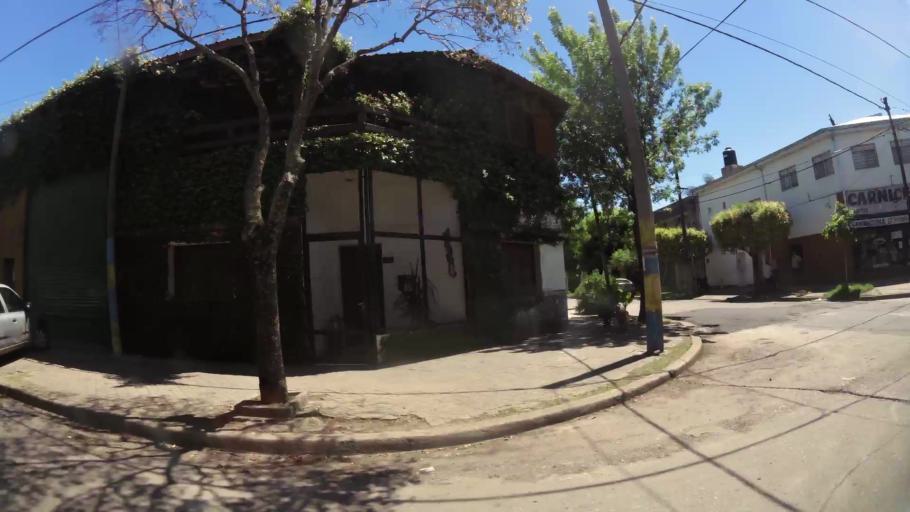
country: AR
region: Santa Fe
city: Perez
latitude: -32.9446
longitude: -60.7148
